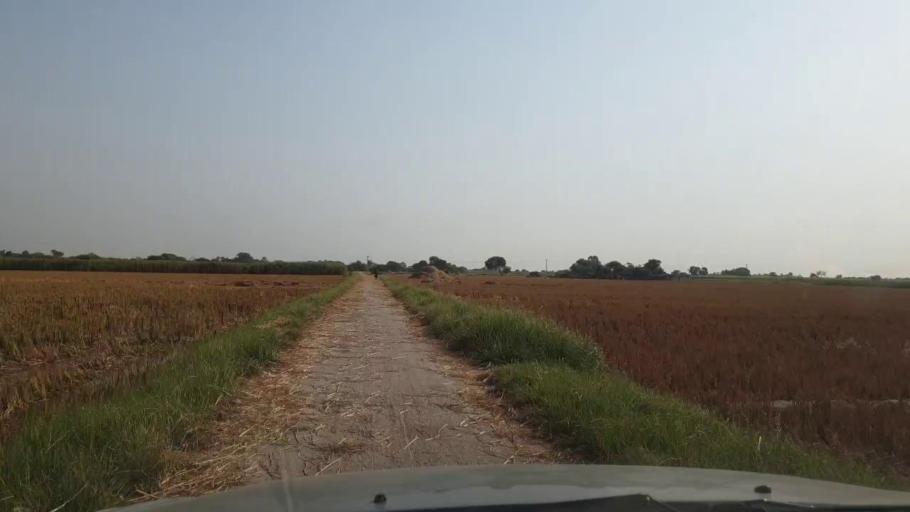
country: PK
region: Sindh
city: Bulri
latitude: 24.9185
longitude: 68.3127
